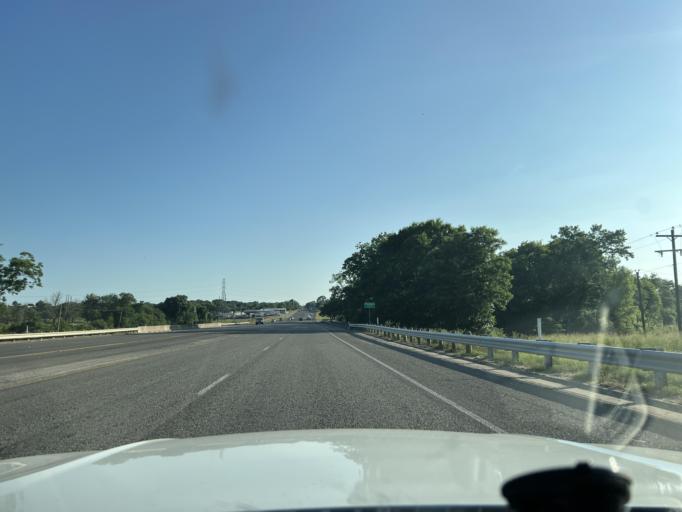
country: US
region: Texas
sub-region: Washington County
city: Brenham
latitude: 30.1848
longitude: -96.3774
